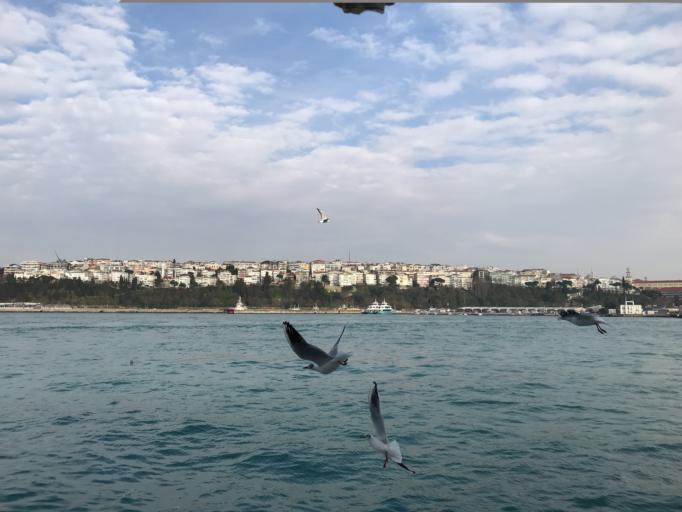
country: TR
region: Istanbul
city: UEskuedar
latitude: 41.0127
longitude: 29.0043
